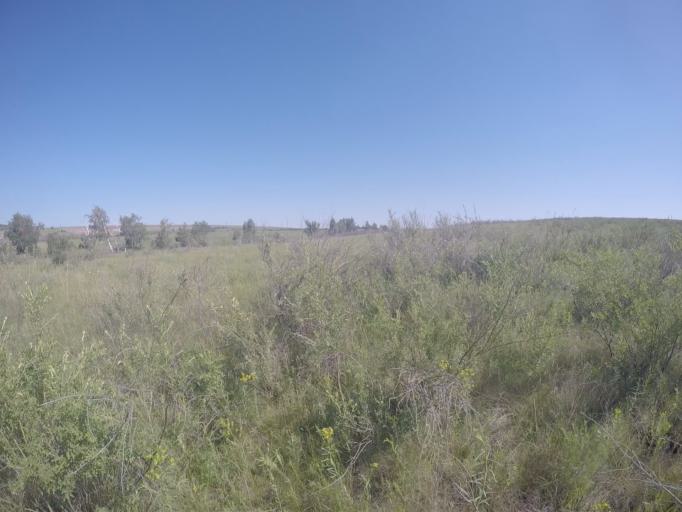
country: RU
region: Saratov
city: Krasnoarmeysk
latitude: 51.2797
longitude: 45.5849
